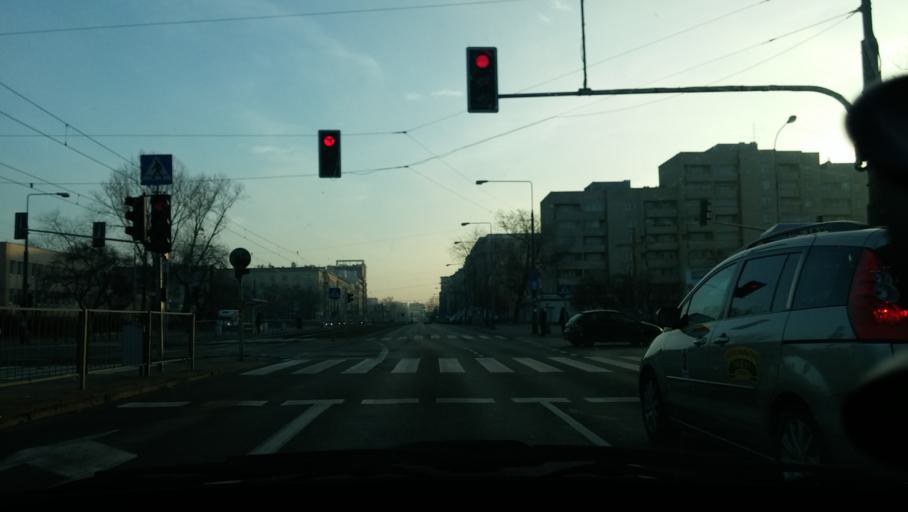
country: PL
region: Masovian Voivodeship
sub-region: Warszawa
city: Praga Poludnie
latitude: 52.2458
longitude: 21.0743
